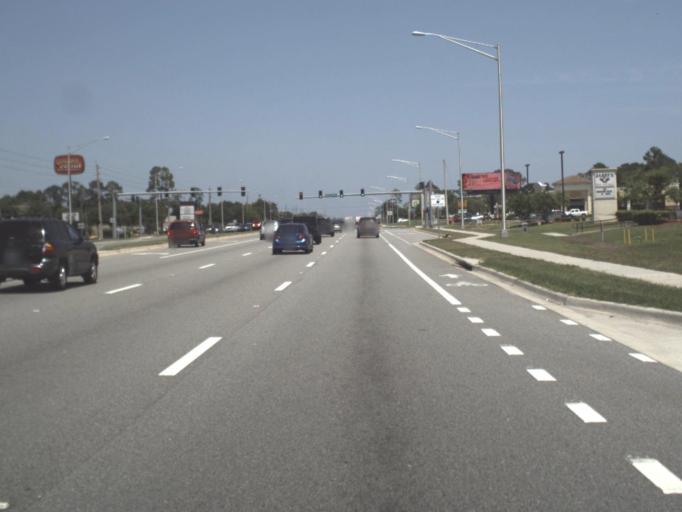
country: US
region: Florida
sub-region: Duval County
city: Jacksonville Beach
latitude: 30.2877
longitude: -81.4500
